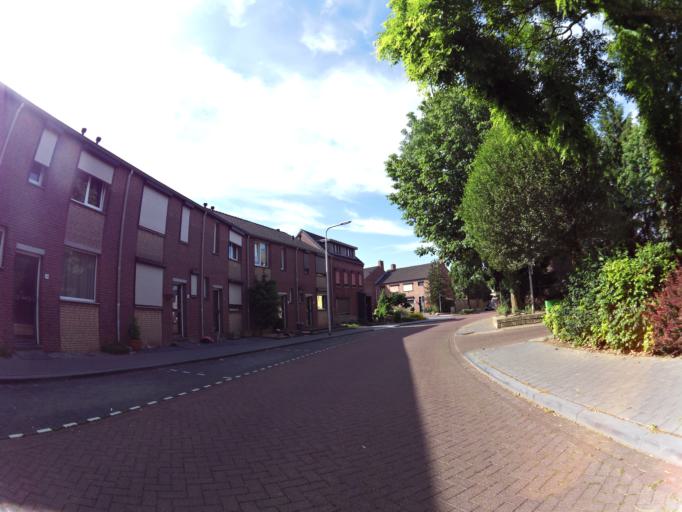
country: NL
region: Limburg
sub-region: Gemeente Kerkrade
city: Kerkrade
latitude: 50.8502
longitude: 6.0706
